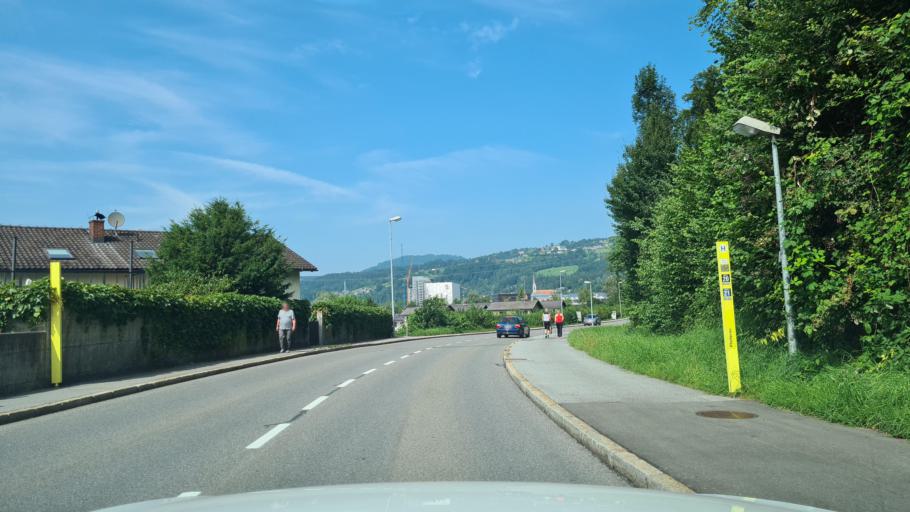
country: AT
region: Vorarlberg
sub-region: Politischer Bezirk Bregenz
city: Schwarzach
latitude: 47.4347
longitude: 9.7562
